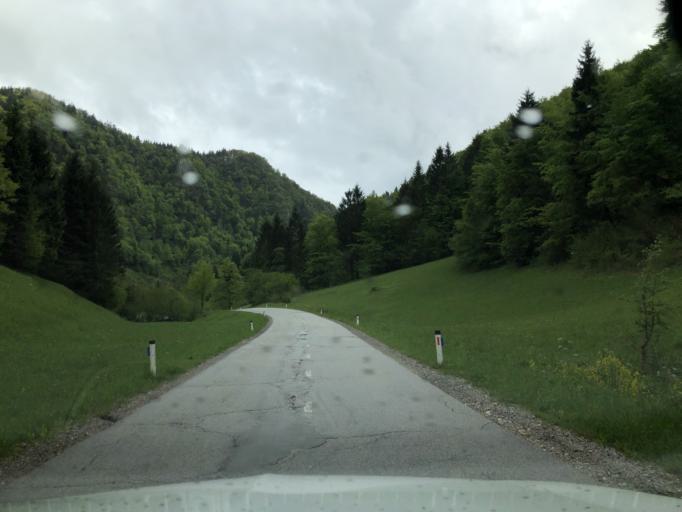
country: SI
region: Jesenice
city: Slovenski Javornik
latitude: 46.4085
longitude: 14.0773
